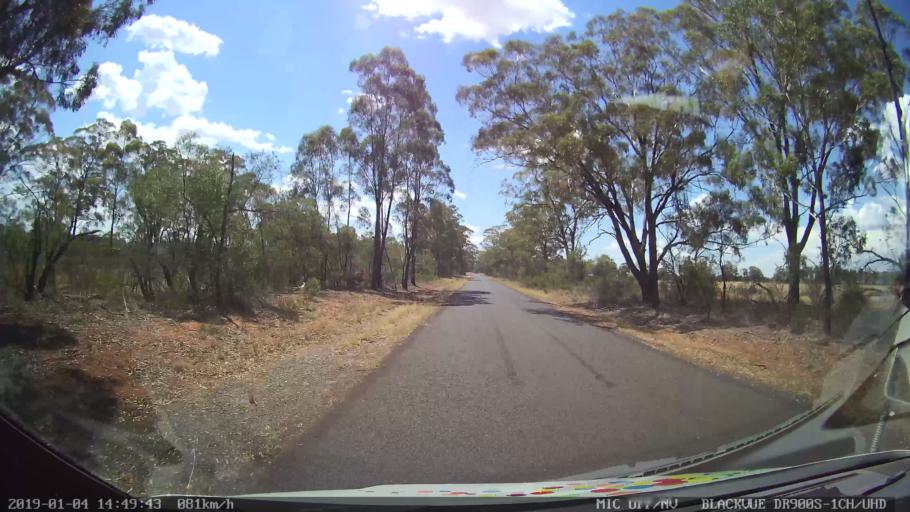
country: AU
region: New South Wales
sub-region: Dubbo Municipality
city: Dubbo
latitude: -32.0461
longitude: 148.6614
